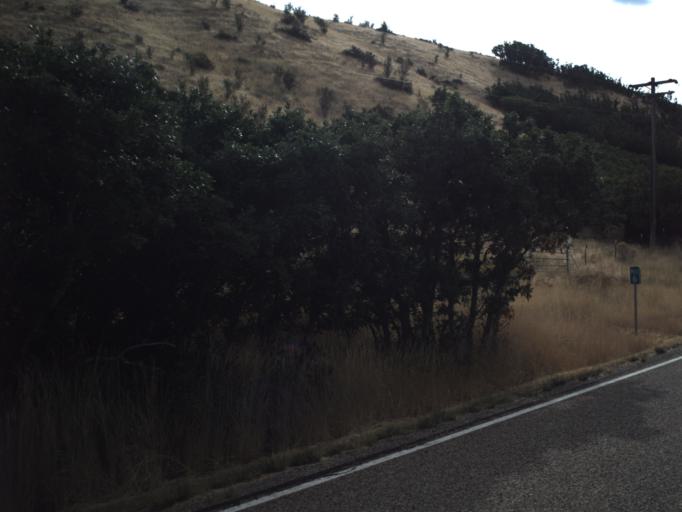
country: US
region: Utah
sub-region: Morgan County
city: Morgan
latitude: 40.9478
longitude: -111.6550
